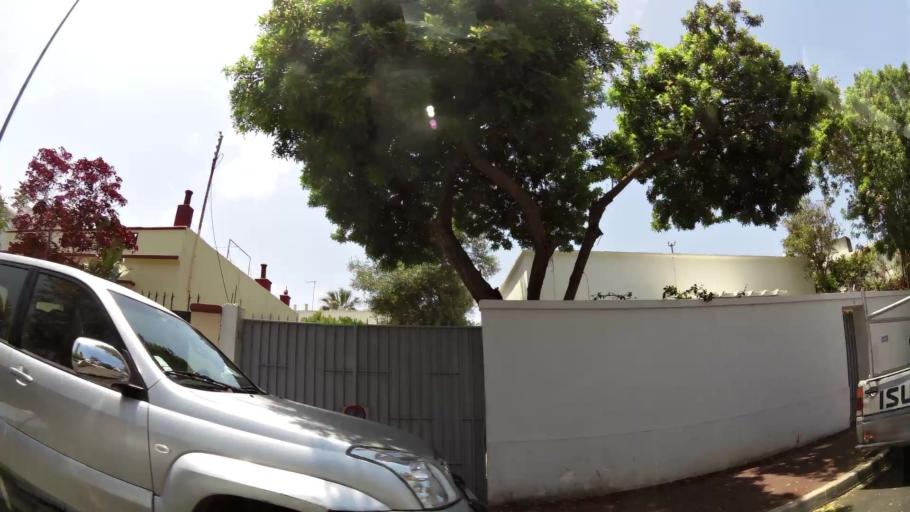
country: MA
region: Rabat-Sale-Zemmour-Zaer
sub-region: Rabat
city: Rabat
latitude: 34.0165
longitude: -6.8268
